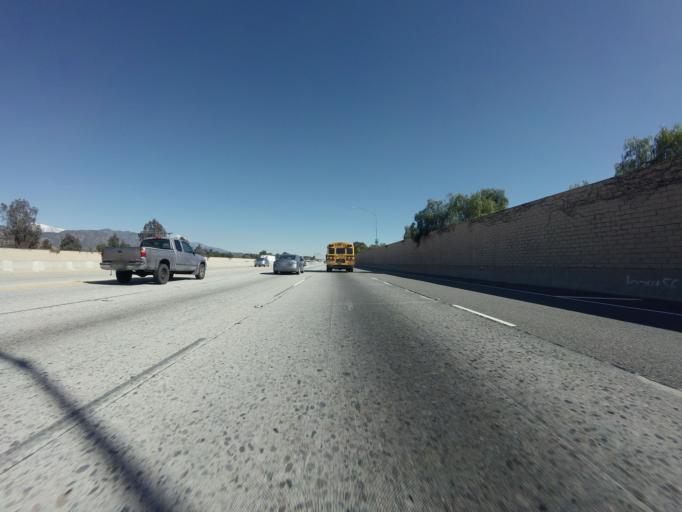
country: US
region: California
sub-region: Los Angeles County
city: La Verne
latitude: 34.1197
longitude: -117.7806
